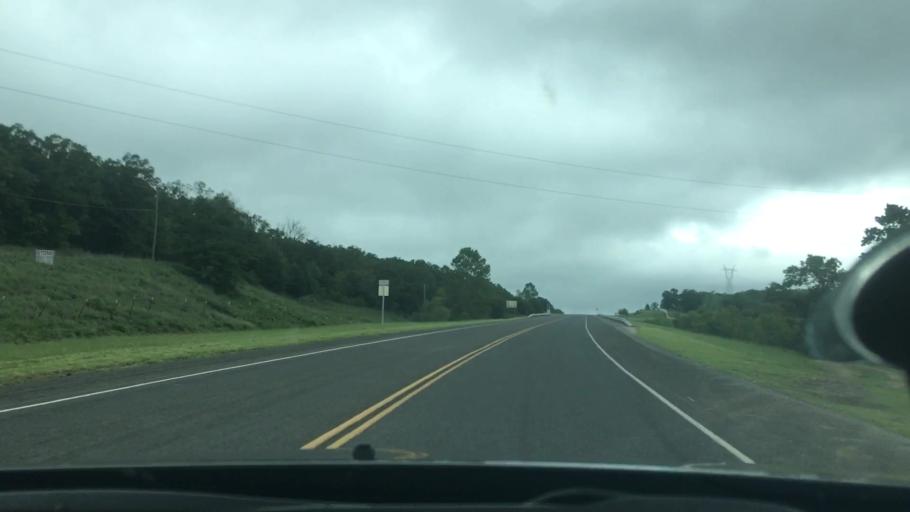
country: US
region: Oklahoma
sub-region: Sequoyah County
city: Vian
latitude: 35.5192
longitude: -94.9733
